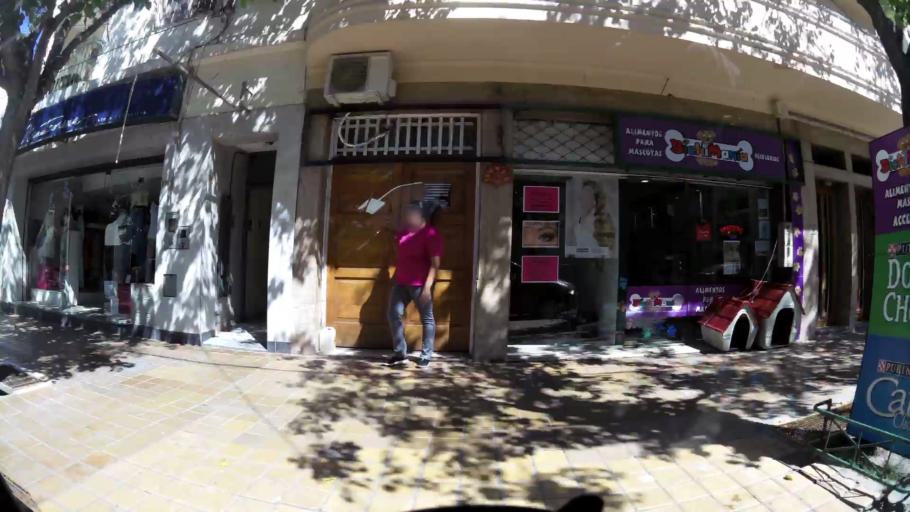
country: AR
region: San Juan
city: San Juan
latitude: -31.5405
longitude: -68.5241
